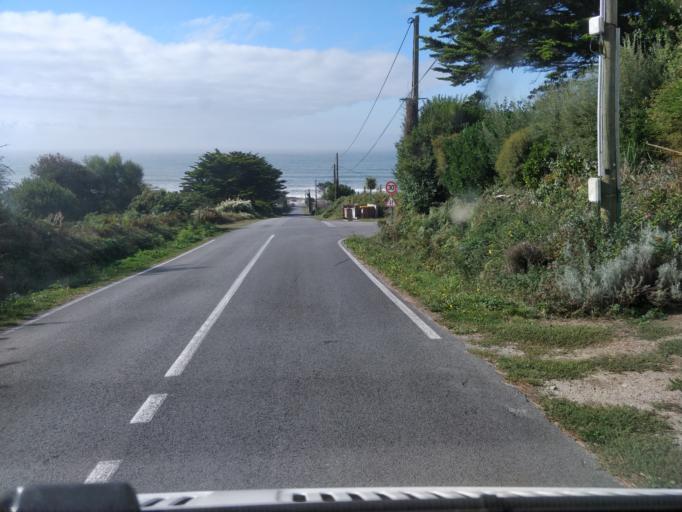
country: FR
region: Brittany
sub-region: Departement du Finistere
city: Plouhinec
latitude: 48.0044
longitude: -4.4968
